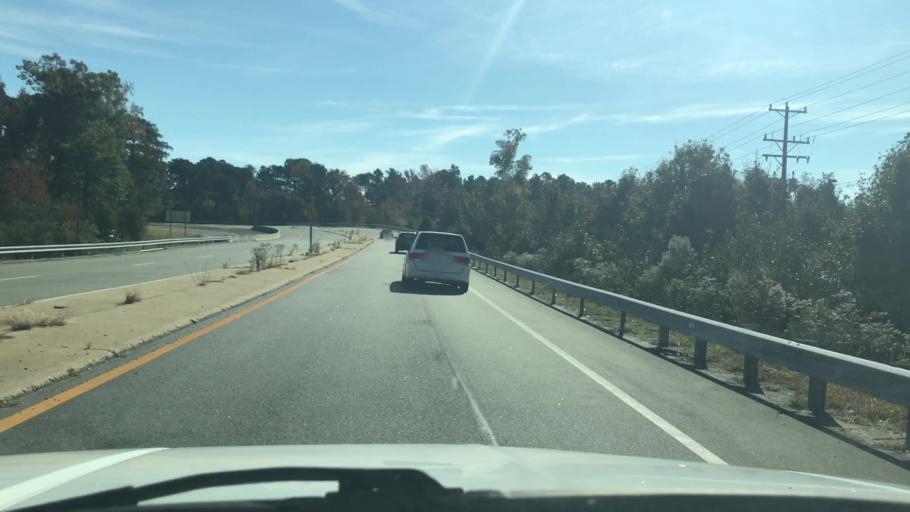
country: US
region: Virginia
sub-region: Henrico County
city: Short Pump
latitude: 37.6477
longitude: -77.5958
